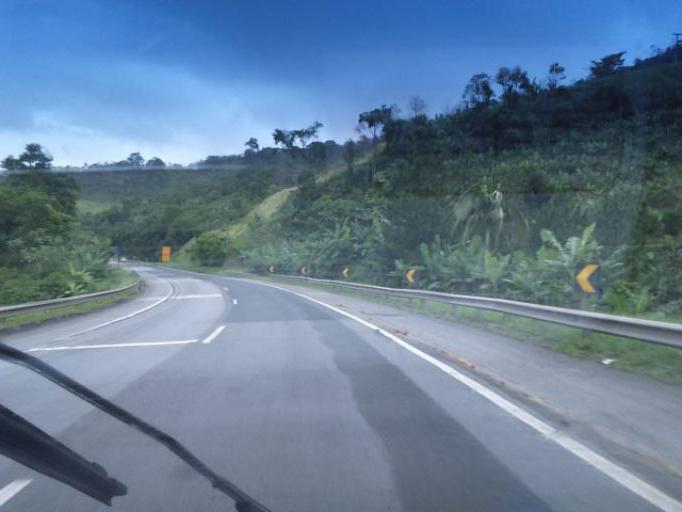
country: BR
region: Sao Paulo
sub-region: Cajati
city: Cajati
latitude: -24.8676
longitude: -48.2105
